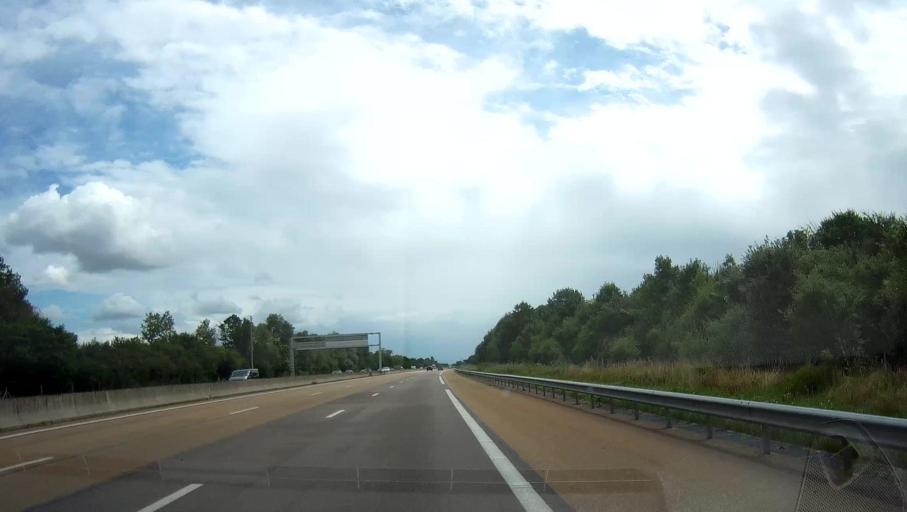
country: FR
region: Bourgogne
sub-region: Departement de la Cote-d'Or
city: Couternon
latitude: 47.3295
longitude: 5.1691
